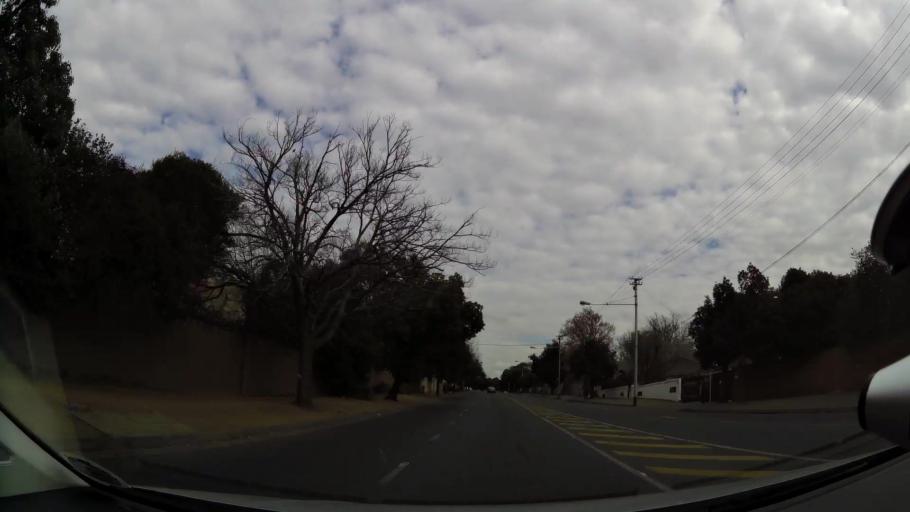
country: ZA
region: Orange Free State
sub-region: Mangaung Metropolitan Municipality
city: Bloemfontein
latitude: -29.0932
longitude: 26.2273
